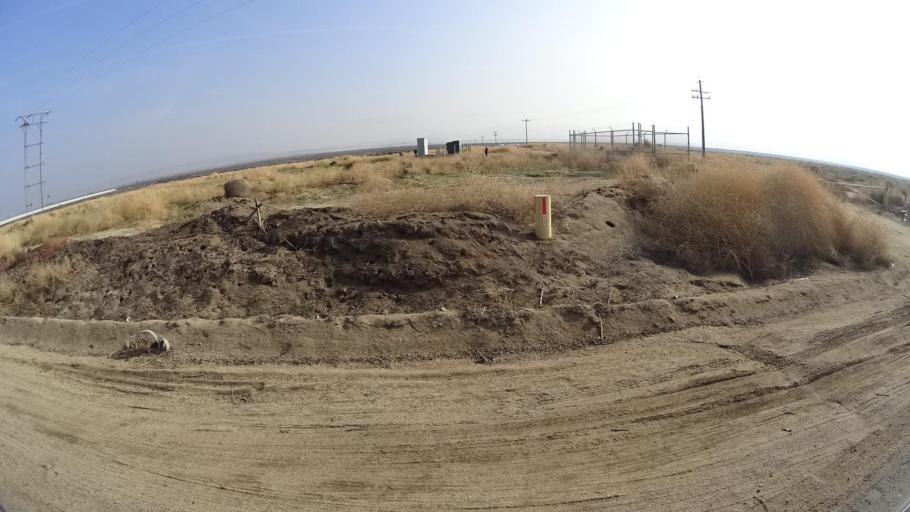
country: US
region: California
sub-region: Kern County
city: Lebec
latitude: 35.0164
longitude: -118.8466
